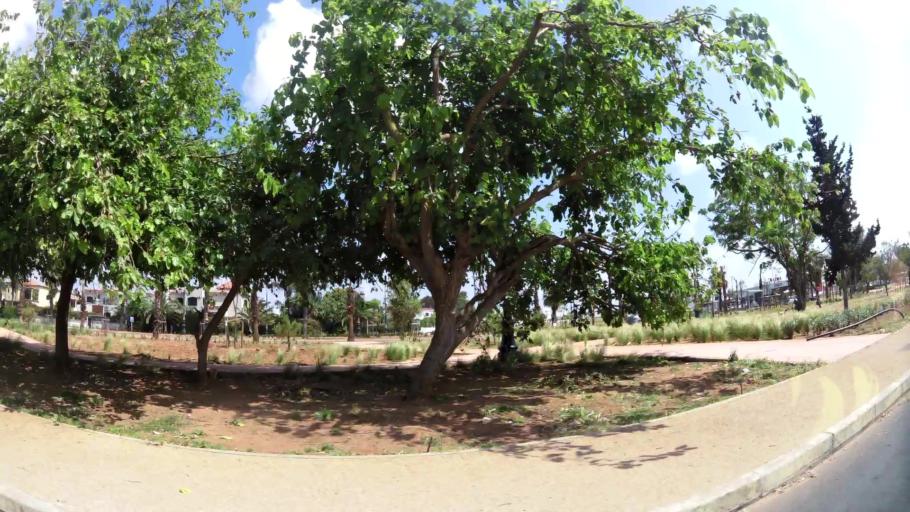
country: MA
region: Rabat-Sale-Zemmour-Zaer
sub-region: Skhirate-Temara
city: Temara
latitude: 33.9551
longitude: -6.8805
